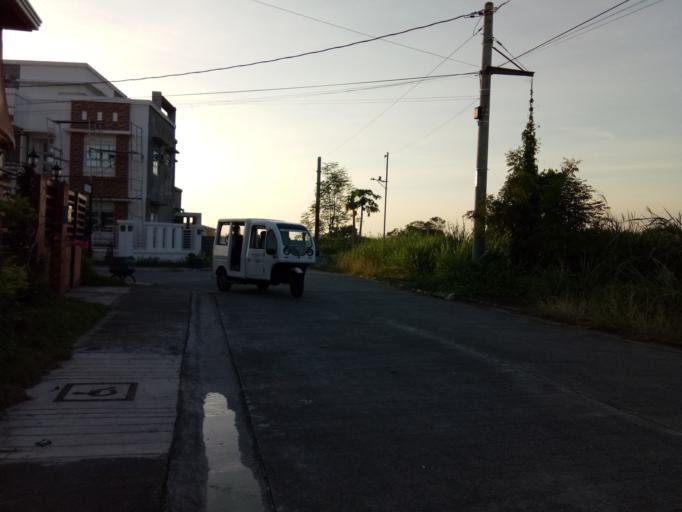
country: PH
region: Calabarzon
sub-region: Province of Cavite
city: Biga
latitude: 14.2780
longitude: 120.9705
